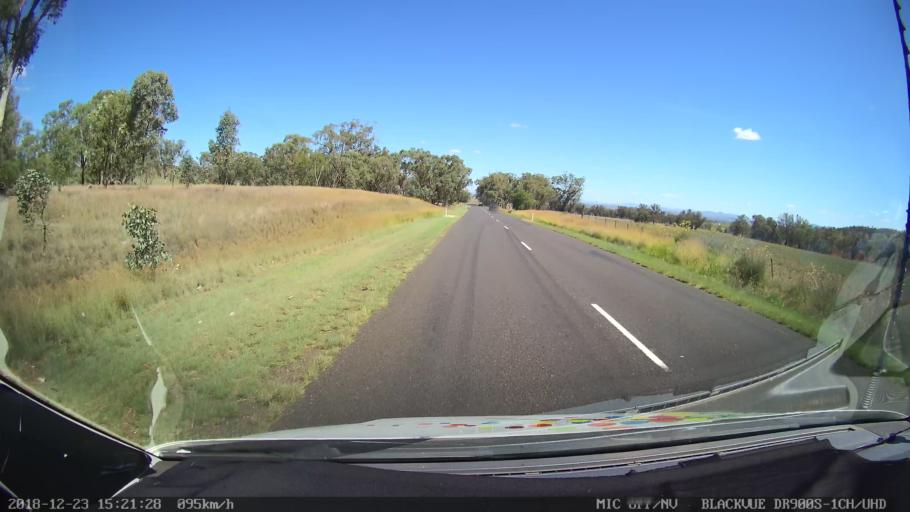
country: AU
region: New South Wales
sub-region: Tamworth Municipality
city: Manilla
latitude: -30.8567
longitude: 150.7968
